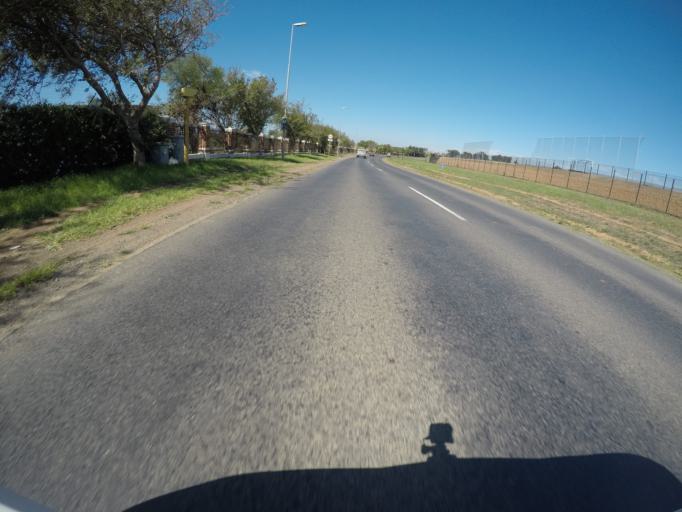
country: ZA
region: Western Cape
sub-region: City of Cape Town
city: Kraaifontein
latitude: -33.8147
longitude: 18.6324
